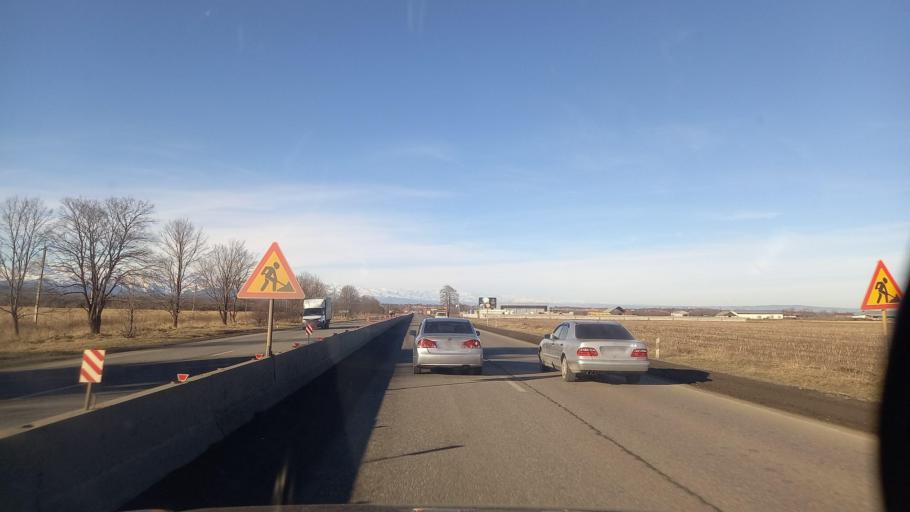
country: RU
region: North Ossetia
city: Vladikavkaz
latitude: 43.0260
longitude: 44.6217
